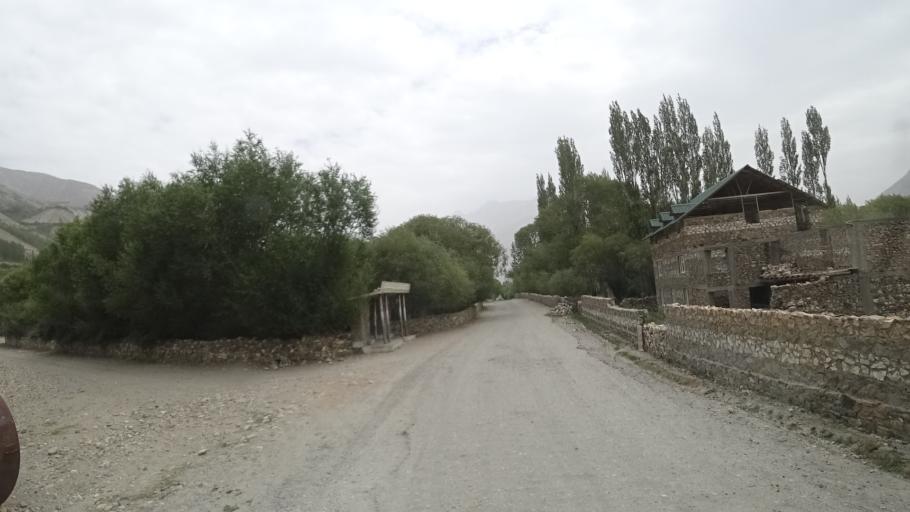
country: AF
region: Badakhshan
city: Khandud
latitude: 37.0298
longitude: 72.6177
